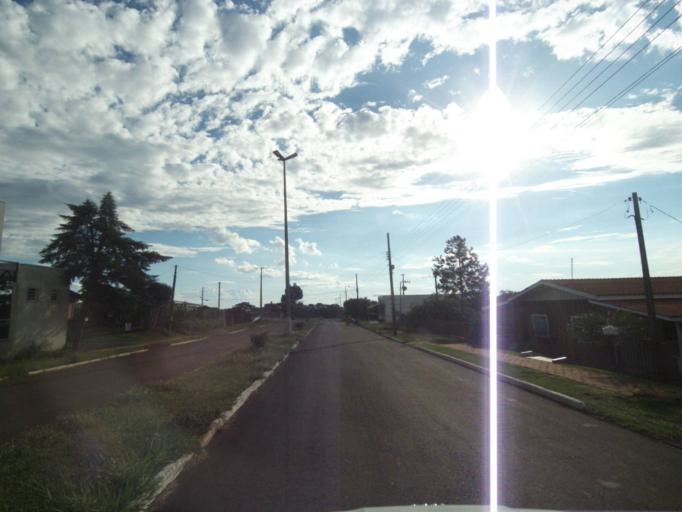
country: BR
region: Parana
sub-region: Laranjeiras Do Sul
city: Laranjeiras do Sul
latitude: -25.4949
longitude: -52.5334
